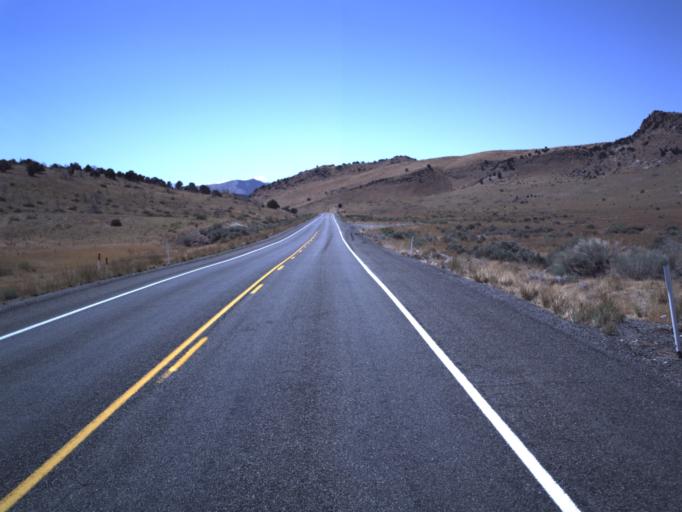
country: US
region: Utah
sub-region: Juab County
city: Nephi
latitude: 39.6555
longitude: -112.0723
